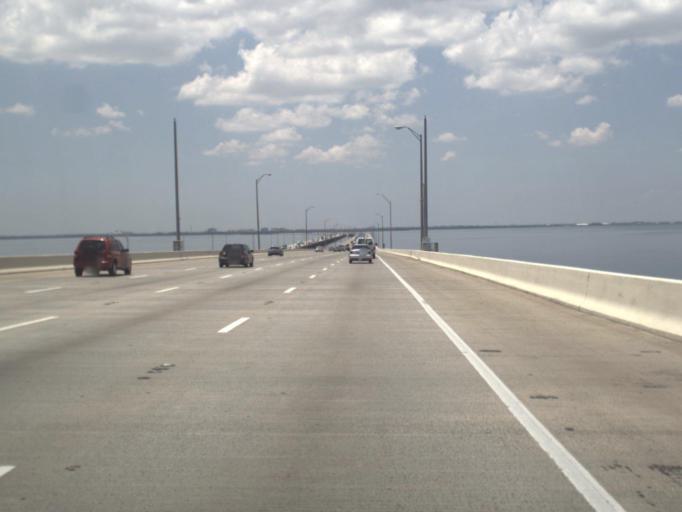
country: US
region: Florida
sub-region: Pinellas County
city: Gandy
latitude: 27.9276
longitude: -82.5893
